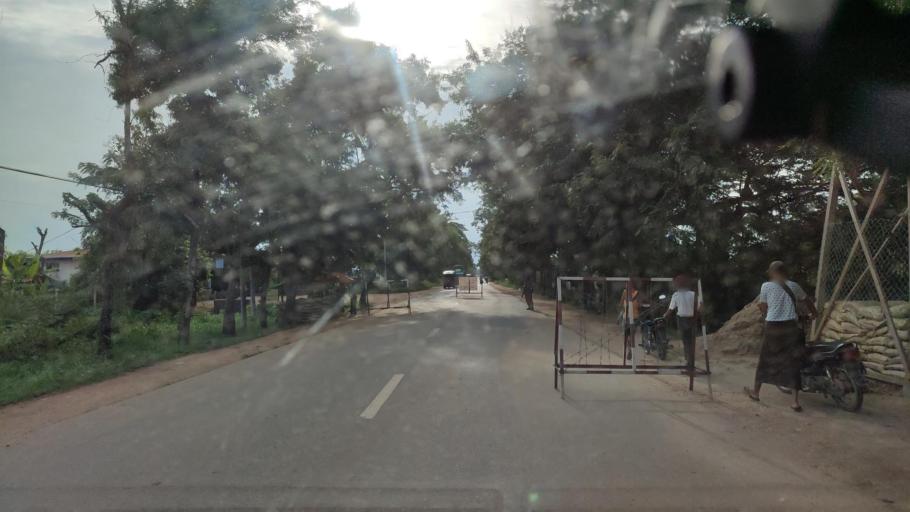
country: MM
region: Bago
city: Paungde
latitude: 18.4980
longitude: 95.4859
